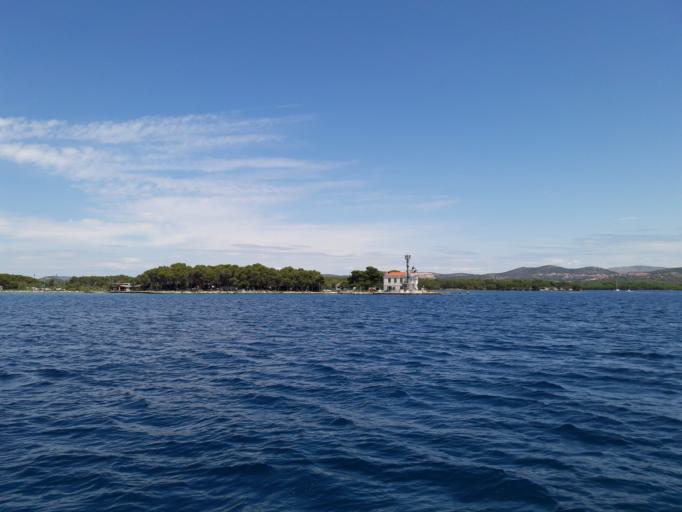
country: HR
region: Sibensko-Kniniska
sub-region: Grad Sibenik
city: Sibenik
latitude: 43.7196
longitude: 15.8486
